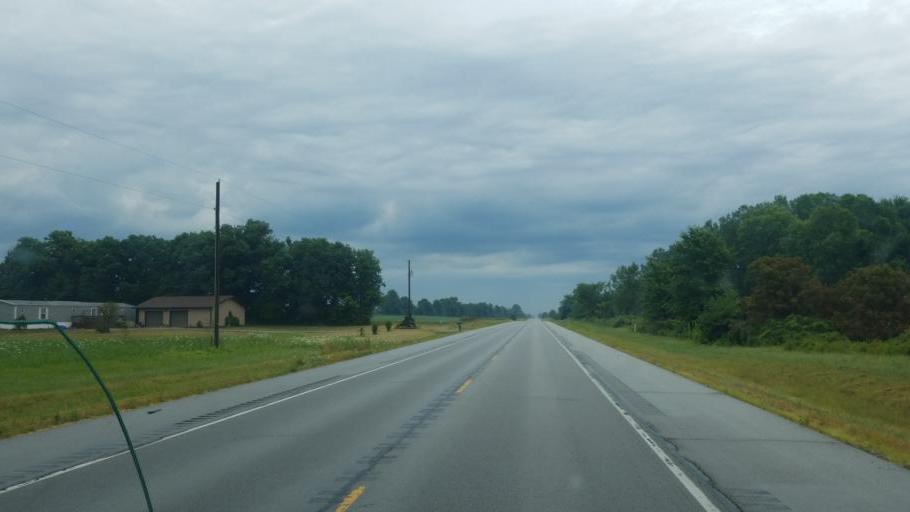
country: US
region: Indiana
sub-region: DeKalb County
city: Butler
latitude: 41.4353
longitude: -84.8248
